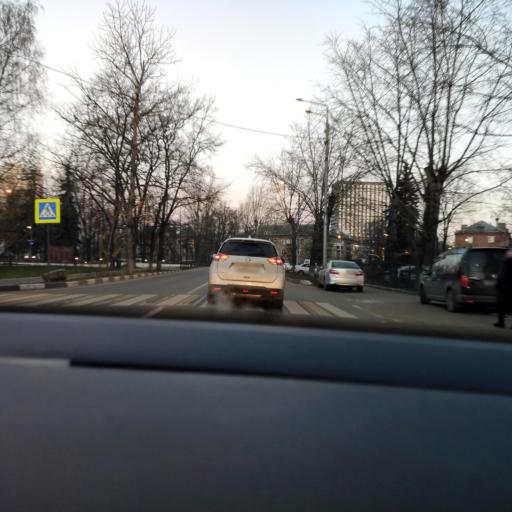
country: RU
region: Moskovskaya
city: Kotel'niki
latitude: 55.6602
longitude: 37.8535
